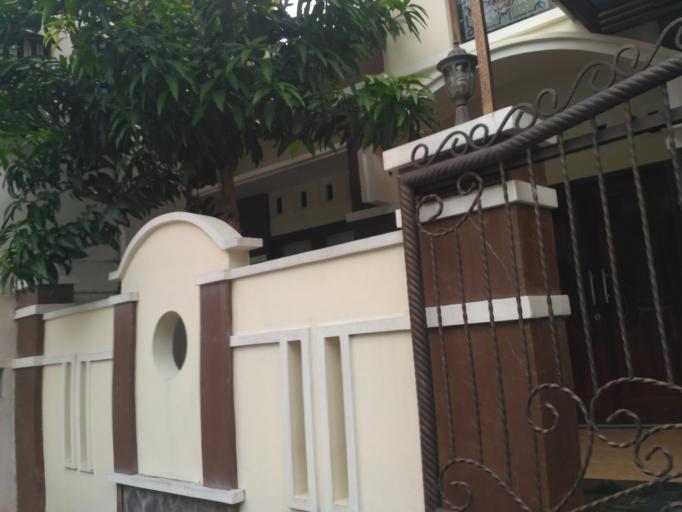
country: ID
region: Central Java
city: Semarang
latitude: -7.0591
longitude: 110.4238
